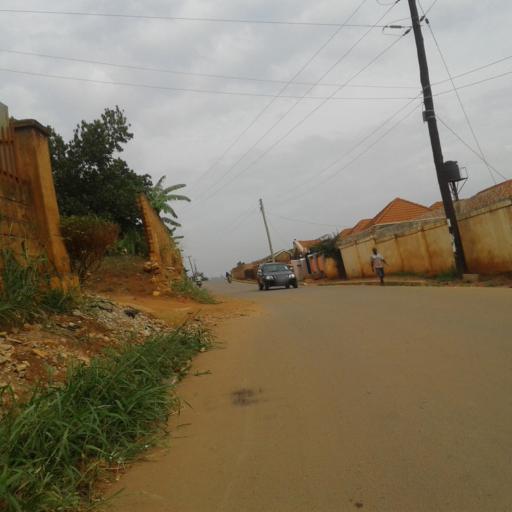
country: UG
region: Central Region
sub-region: Kampala District
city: Kampala
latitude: 0.2761
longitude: 32.6256
